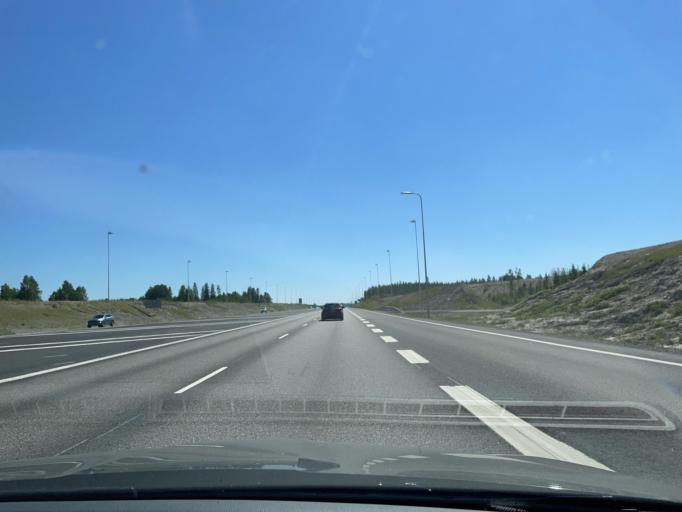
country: FI
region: Central Finland
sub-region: Jyvaeskylae
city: Jyvaeskylae
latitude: 62.4056
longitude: 25.6984
